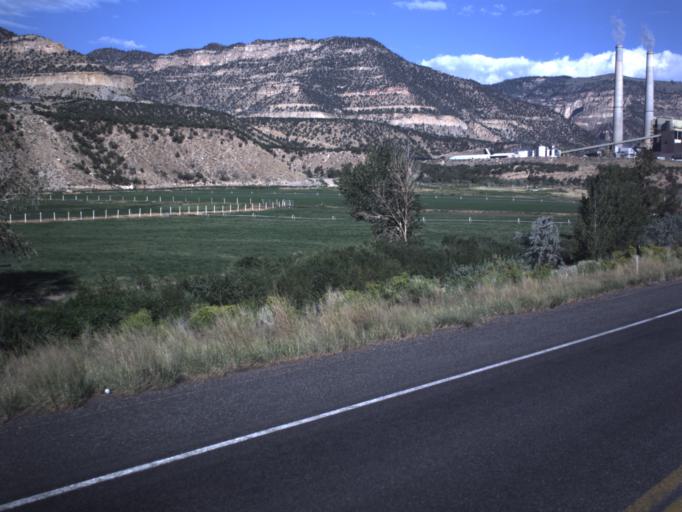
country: US
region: Utah
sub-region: Emery County
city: Huntington
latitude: 39.3742
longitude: -111.0638
